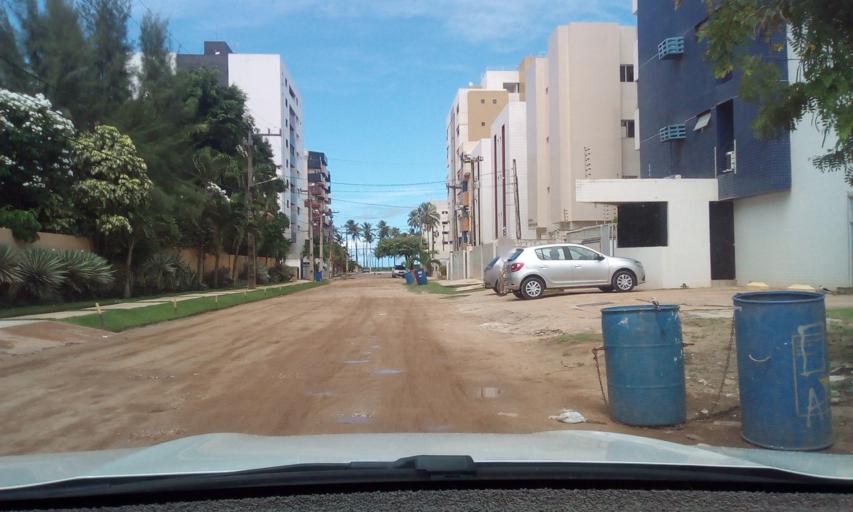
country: BR
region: Paraiba
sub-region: Cabedelo
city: Cabedelo
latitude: -7.0370
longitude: -34.8403
